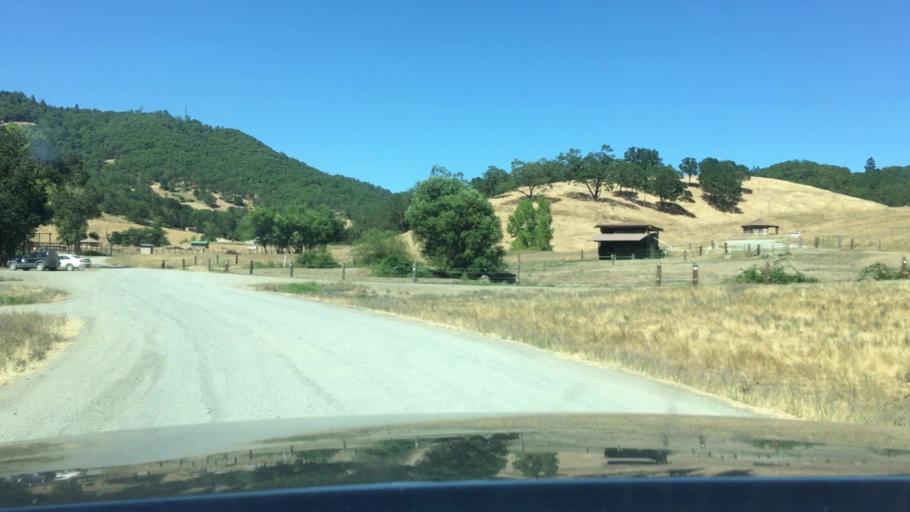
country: US
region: Oregon
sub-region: Douglas County
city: Winston
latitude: 43.1348
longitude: -123.4329
